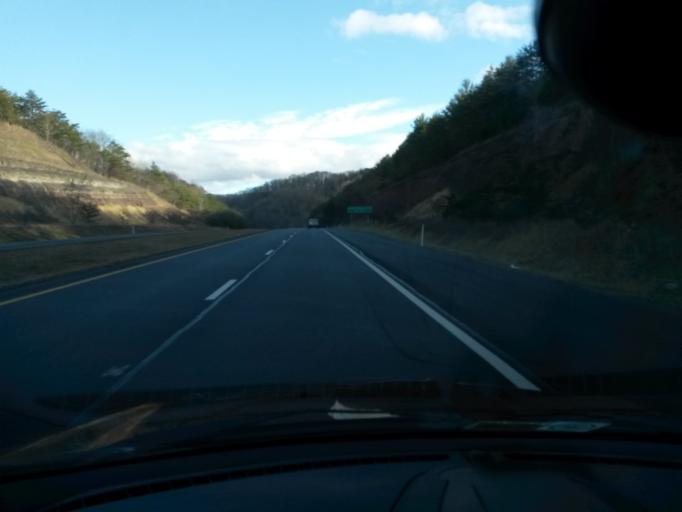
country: US
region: West Virginia
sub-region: Mercer County
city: Athens
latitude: 37.3413
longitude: -80.9779
